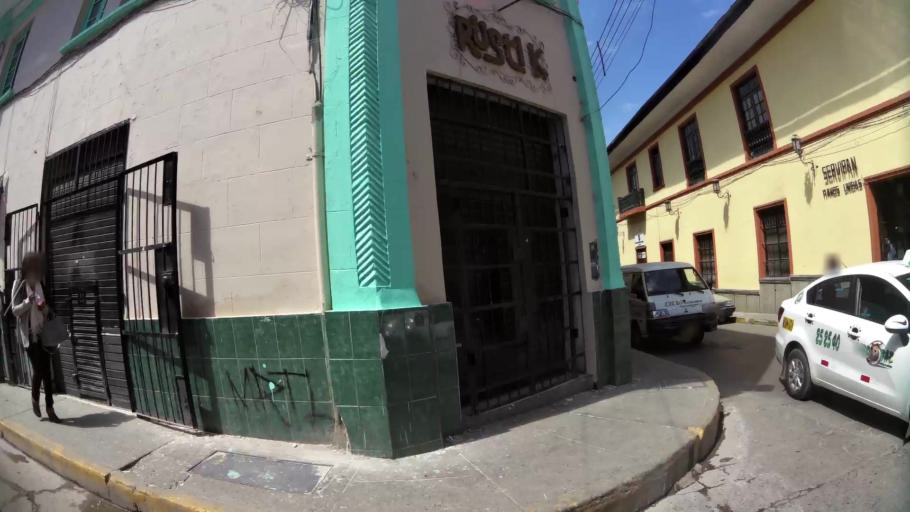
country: PE
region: Junin
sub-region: Provincia de Huancayo
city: El Tambo
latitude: -12.0700
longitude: -75.2106
